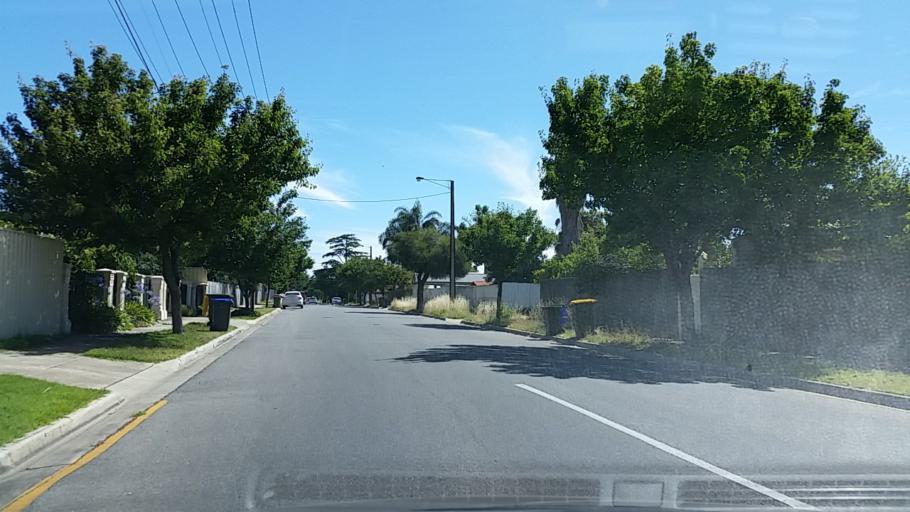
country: AU
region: South Australia
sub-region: Charles Sturt
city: Allenby Gardens
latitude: -34.8890
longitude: 138.5621
